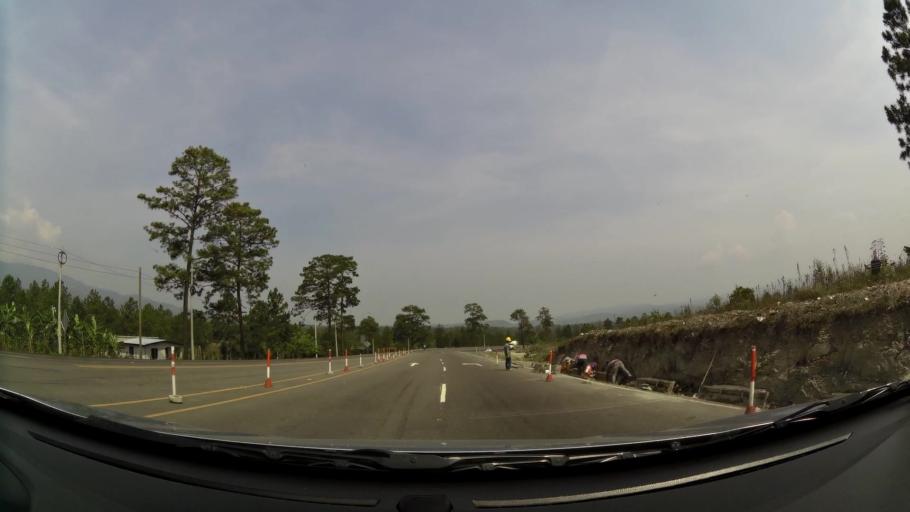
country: HN
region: Comayagua
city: Siguatepeque
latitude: 14.5639
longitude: -87.8286
